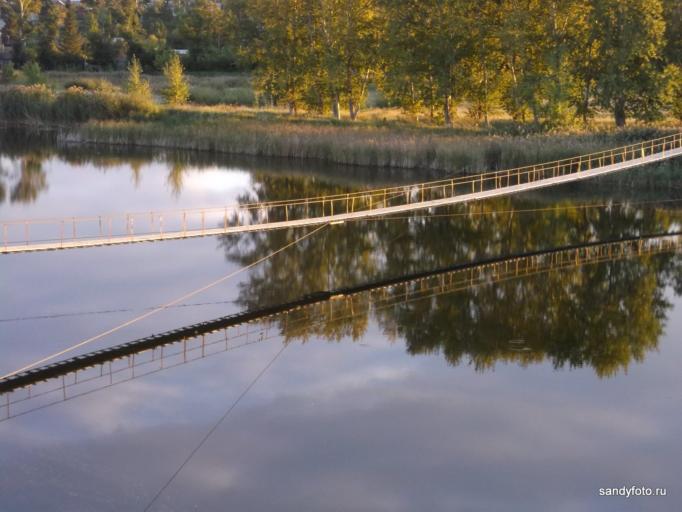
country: RU
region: Chelyabinsk
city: Troitsk
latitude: 54.0689
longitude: 61.5287
